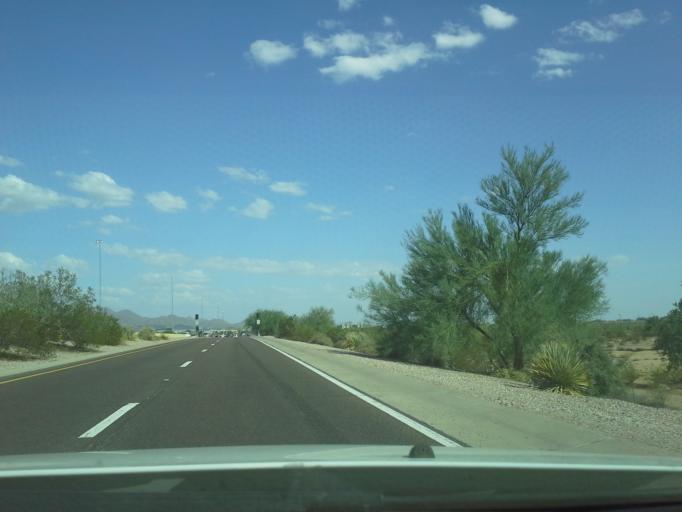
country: US
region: Arizona
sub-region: Maricopa County
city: Paradise Valley
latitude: 33.6663
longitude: -111.9576
